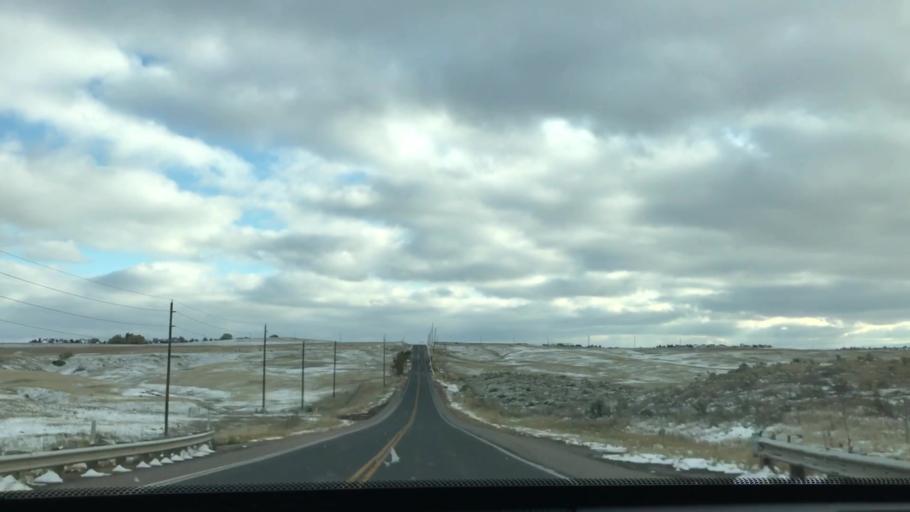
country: US
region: Colorado
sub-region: Boulder County
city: Lafayette
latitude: 39.9665
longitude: -105.0719
